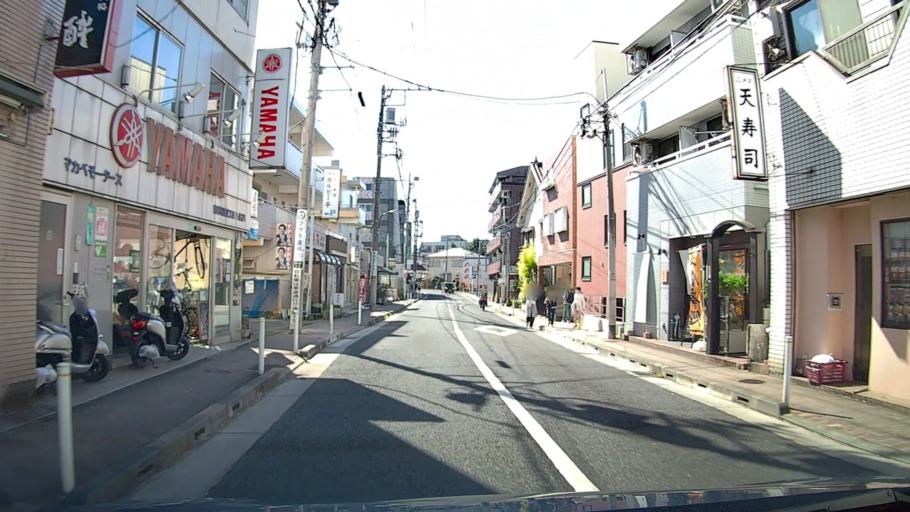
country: JP
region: Saitama
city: Wako
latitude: 35.7520
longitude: 139.5940
